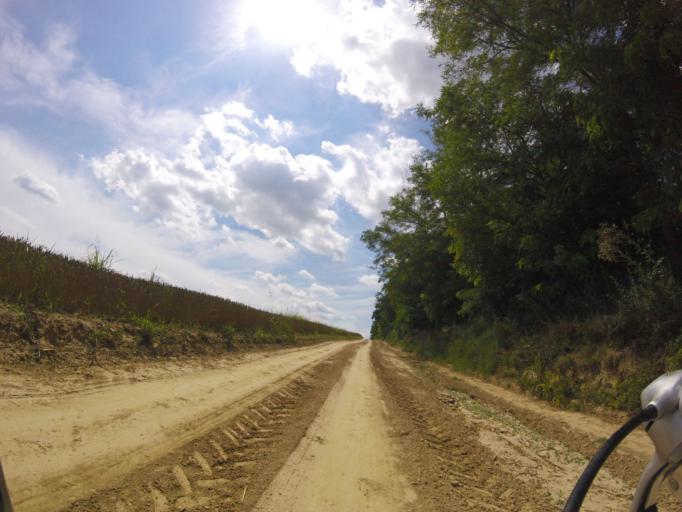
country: HU
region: Somogy
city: Tab
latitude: 46.6874
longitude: 18.0322
